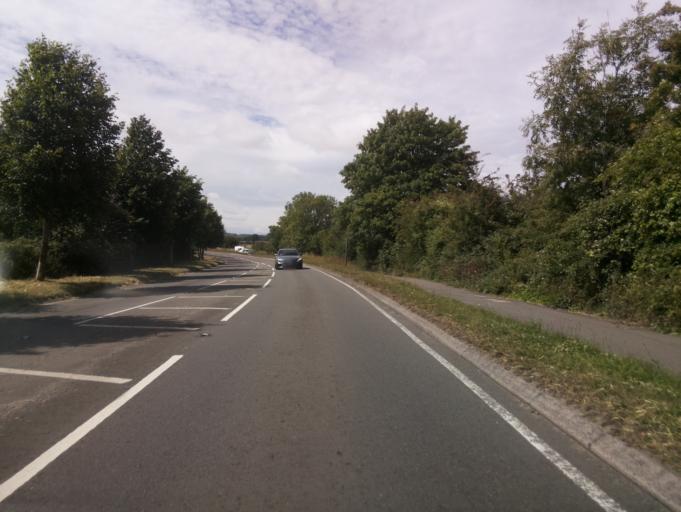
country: GB
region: England
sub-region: Dorset
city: Dorchester
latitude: 50.7196
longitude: -2.4429
